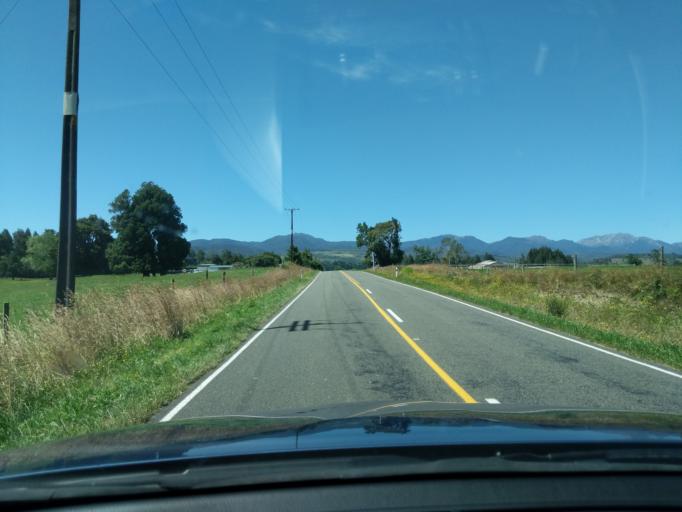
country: NZ
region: Tasman
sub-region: Tasman District
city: Takaka
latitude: -40.7048
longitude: 172.6360
